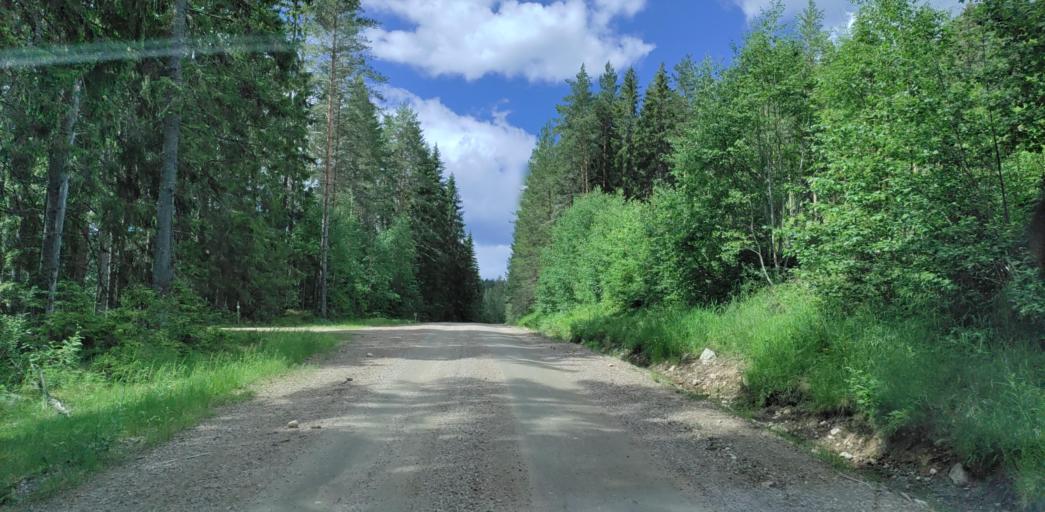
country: SE
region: Vaermland
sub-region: Hagfors Kommun
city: Ekshaerad
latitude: 60.0972
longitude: 13.3993
